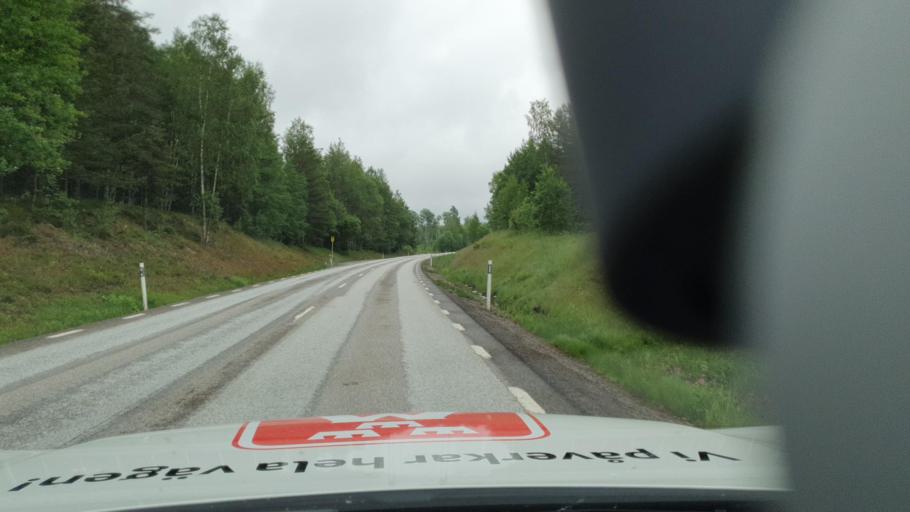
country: SE
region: Vaermland
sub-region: Kristinehamns Kommun
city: Bjorneborg
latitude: 59.2523
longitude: 14.1992
